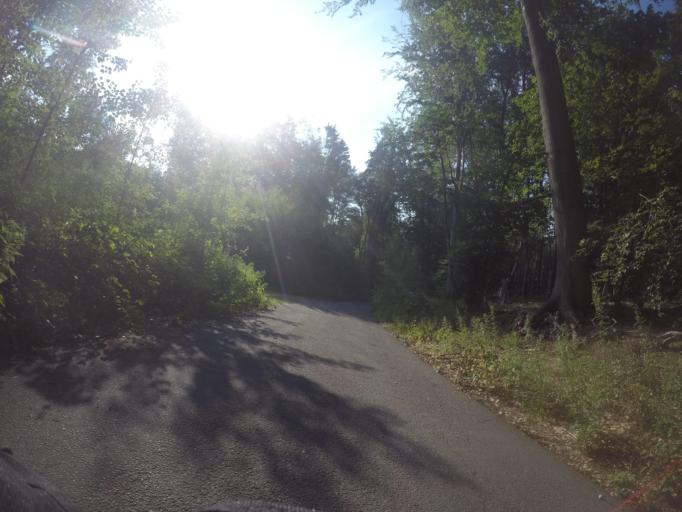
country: DE
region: Lower Saxony
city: Dahlenburg
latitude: 53.2051
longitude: 10.7289
